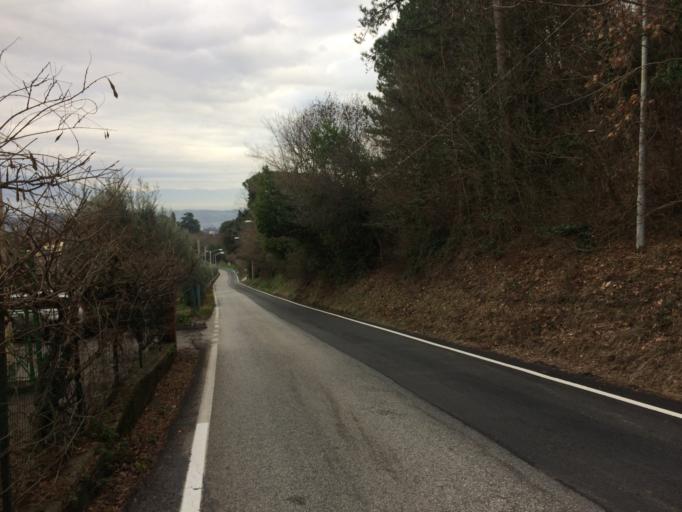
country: IT
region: Umbria
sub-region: Provincia di Perugia
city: Perugia
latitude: 43.1038
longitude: 12.3992
